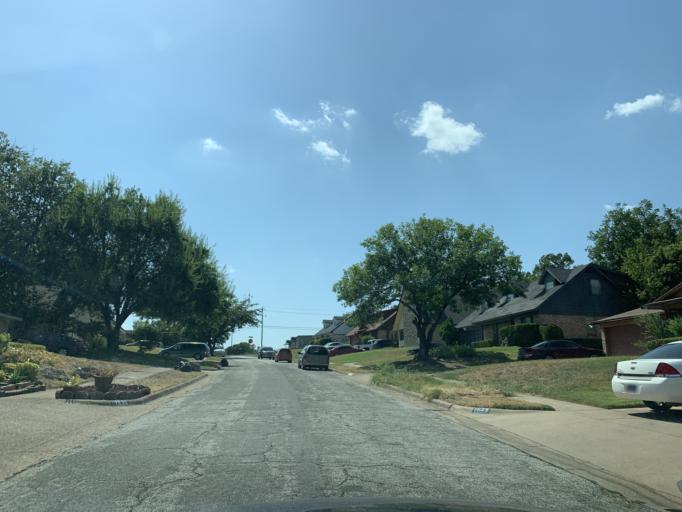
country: US
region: Texas
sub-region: Dallas County
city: Hutchins
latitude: 32.6741
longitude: -96.7951
